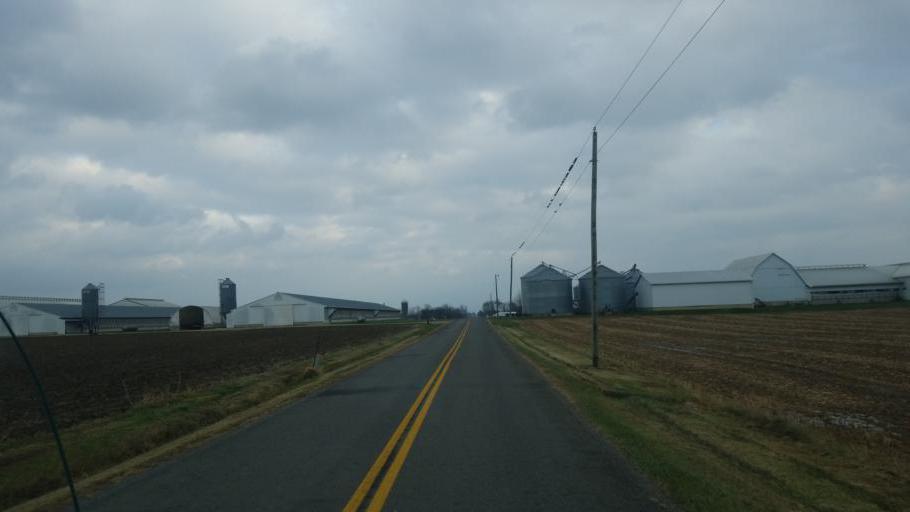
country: US
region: Ohio
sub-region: Mercer County
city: Fort Recovery
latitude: 40.5090
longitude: -84.7569
